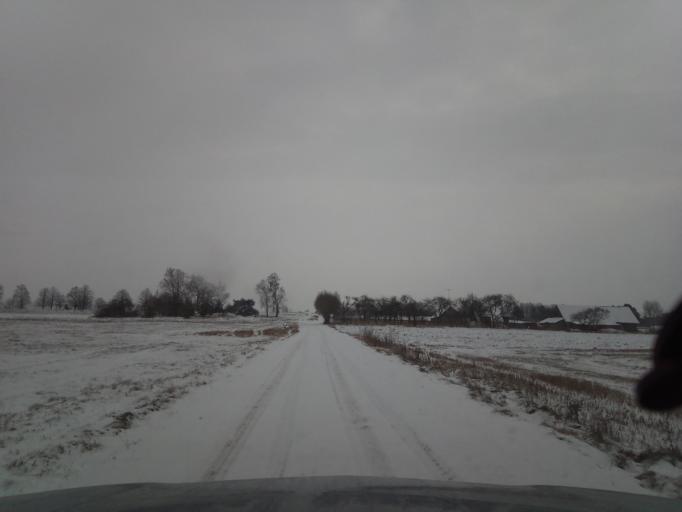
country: LT
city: Ramygala
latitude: 55.6034
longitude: 24.3427
